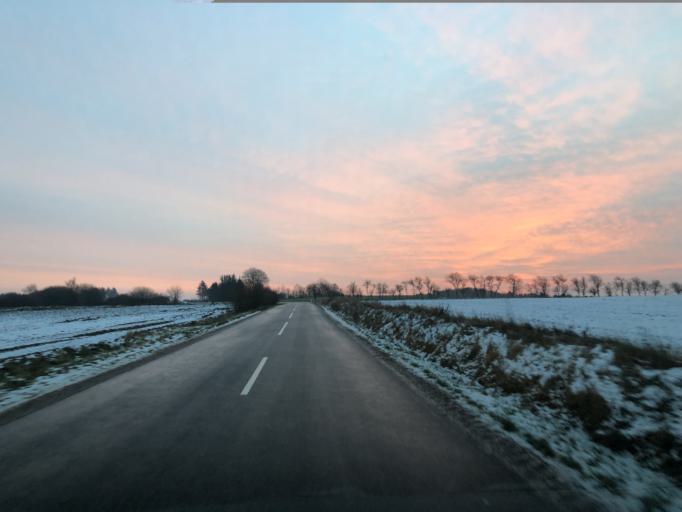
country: DK
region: Central Jutland
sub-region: Holstebro Kommune
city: Ulfborg
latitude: 56.2009
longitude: 8.4444
